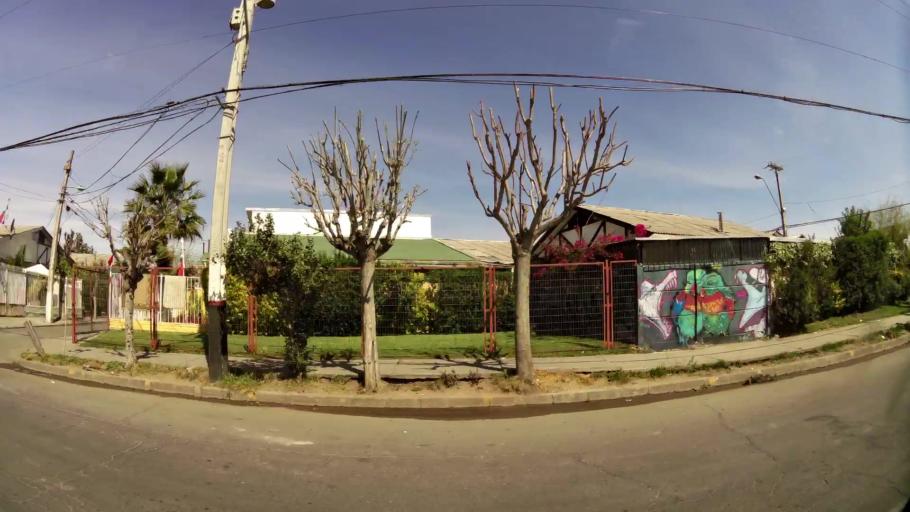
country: CL
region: Santiago Metropolitan
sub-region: Provincia de Cordillera
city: Puente Alto
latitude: -33.5648
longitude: -70.5819
